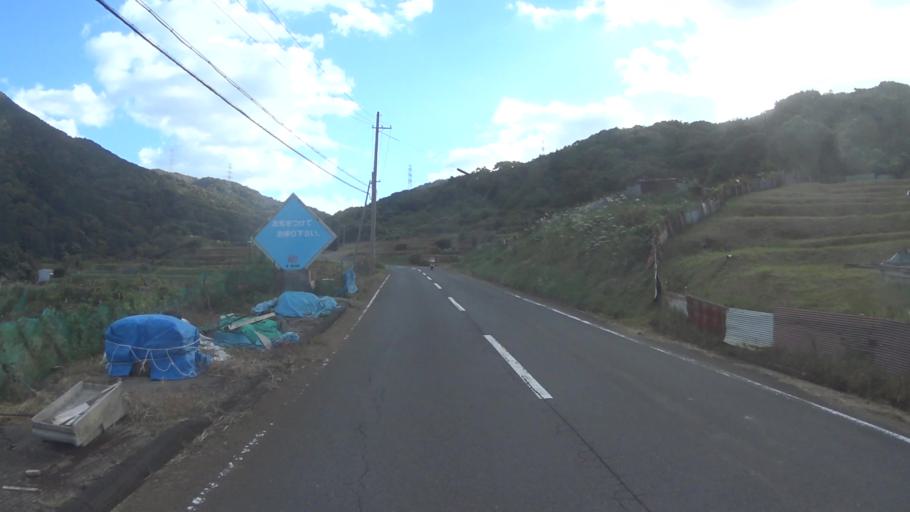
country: JP
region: Kyoto
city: Maizuru
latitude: 35.5537
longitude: 135.3957
